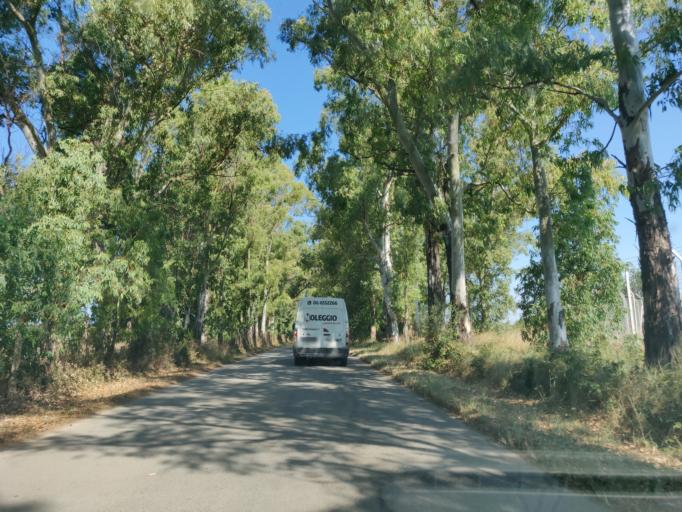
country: IT
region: Latium
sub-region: Citta metropolitana di Roma Capitale
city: Aurelia
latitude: 42.1643
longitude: 11.7433
